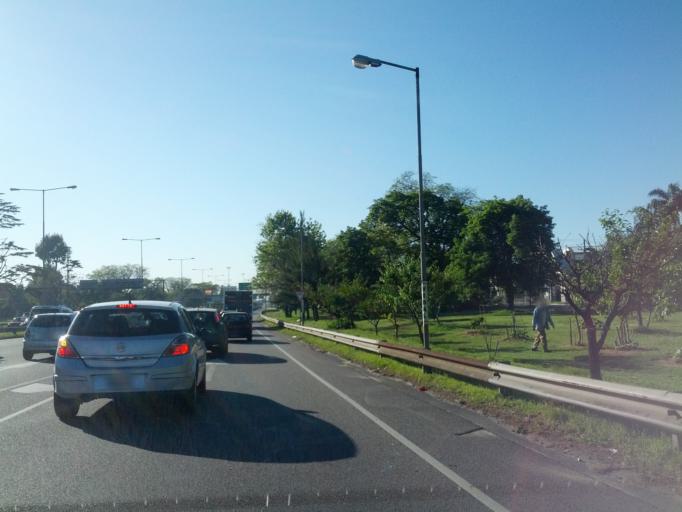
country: AR
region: Buenos Aires
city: San Justo
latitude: -34.6581
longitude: -58.5237
